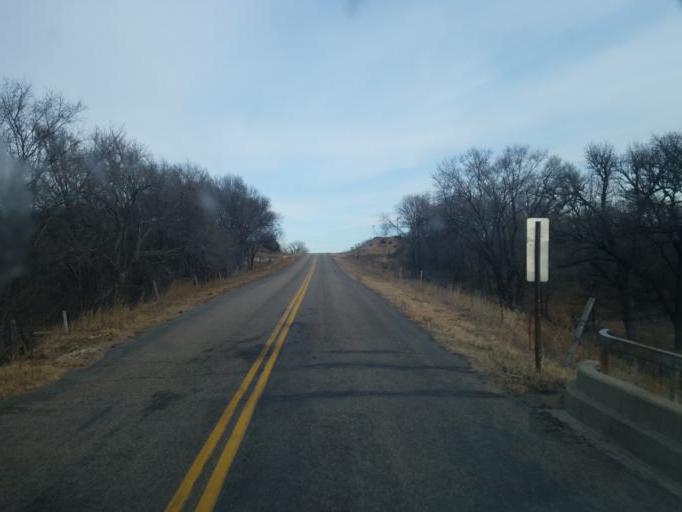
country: US
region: Nebraska
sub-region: Knox County
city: Creighton
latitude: 42.4664
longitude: -98.1155
